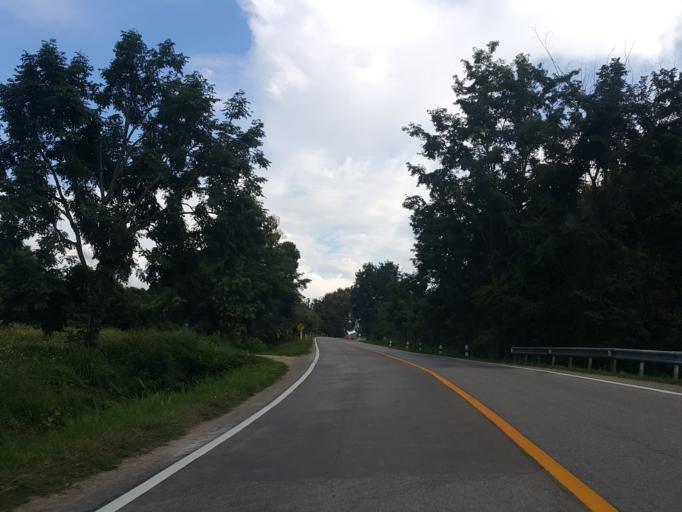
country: TH
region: Chiang Mai
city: Phrao
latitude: 19.2828
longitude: 99.1877
